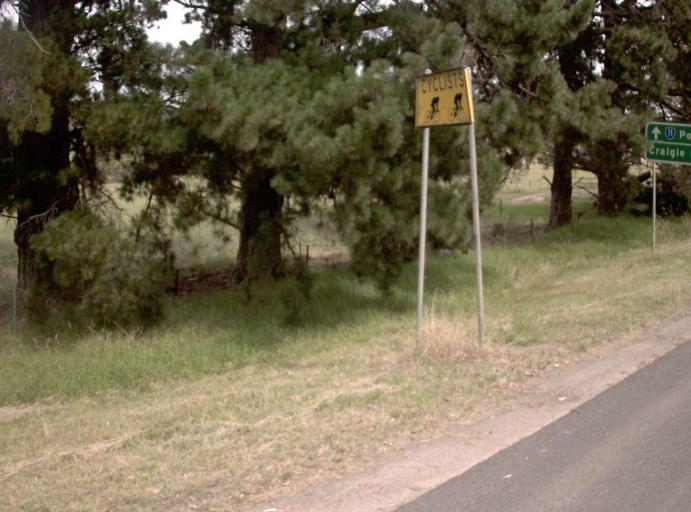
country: AU
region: Victoria
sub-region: Mornington Peninsula
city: Mornington
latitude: -38.2634
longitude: 145.0742
